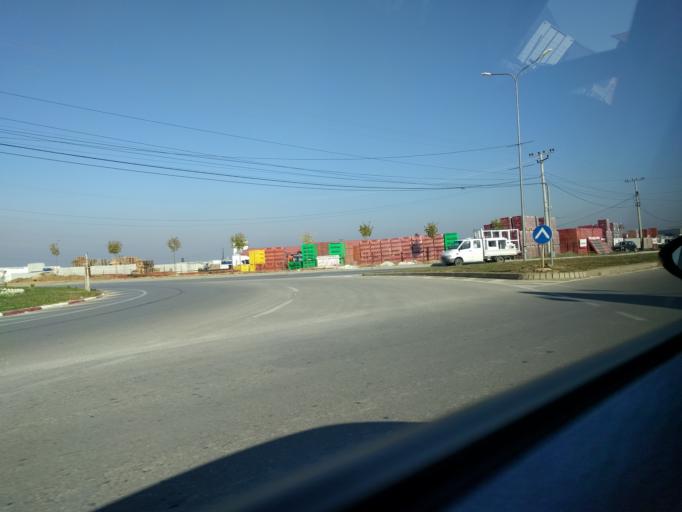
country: XK
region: Prizren
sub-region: Prizren
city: Prizren
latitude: 42.2342
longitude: 20.7588
